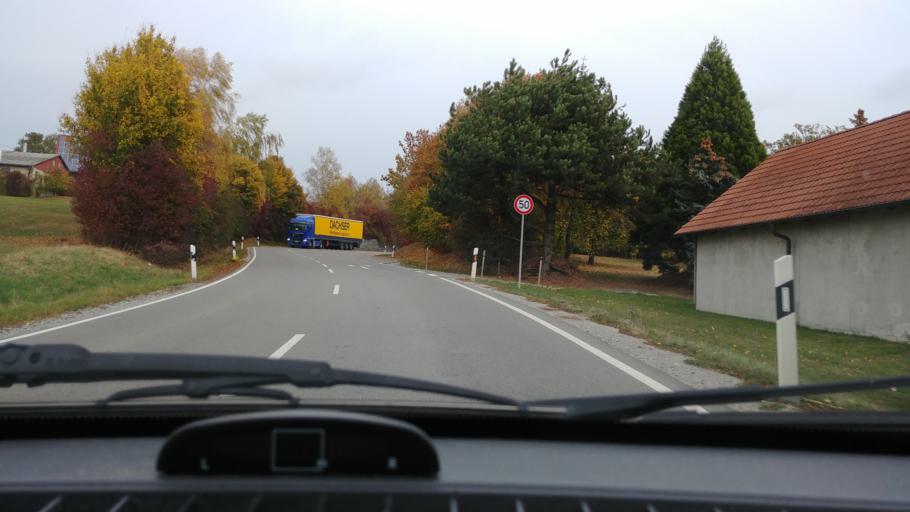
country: DE
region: Baden-Wuerttemberg
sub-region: Regierungsbezirk Stuttgart
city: Satteldorf
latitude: 49.1528
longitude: 10.0747
